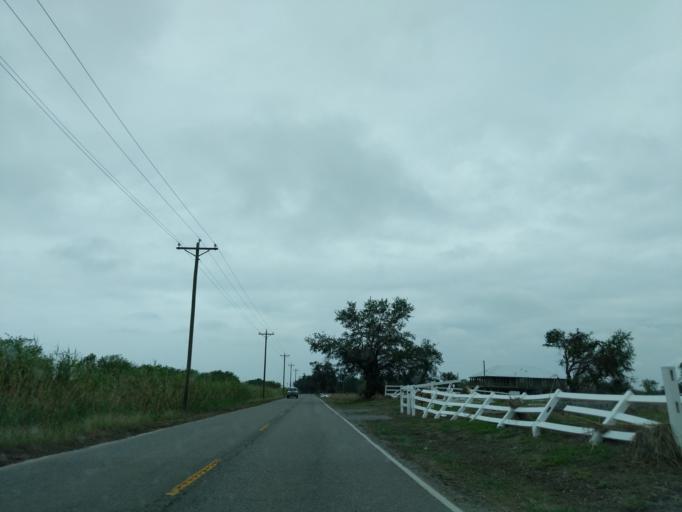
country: US
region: Louisiana
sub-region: Jefferson Davis Parish
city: Lake Arthur
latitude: 29.7515
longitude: -92.9066
